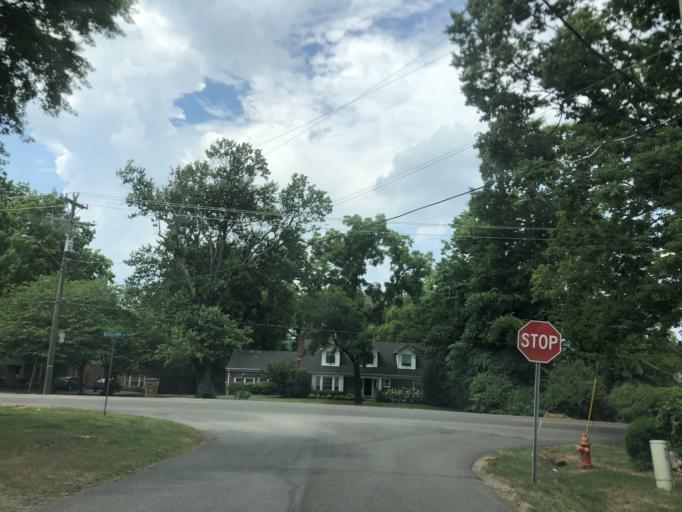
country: US
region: Tennessee
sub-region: Davidson County
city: Belle Meade
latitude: 36.1233
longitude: -86.8229
